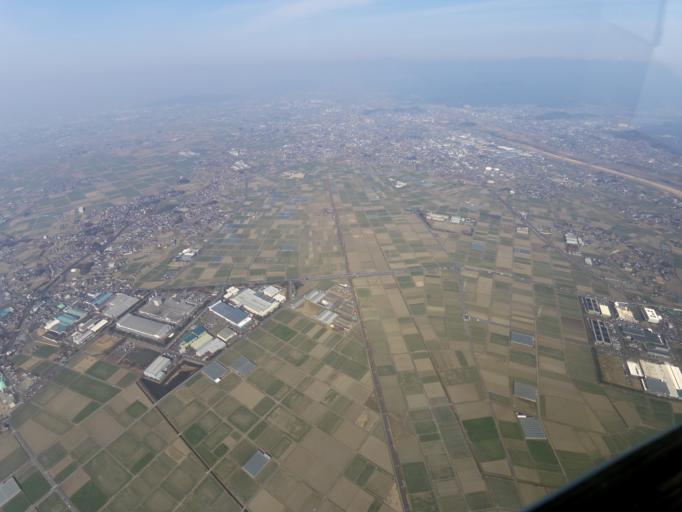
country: JP
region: Tochigi
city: Ashikaga
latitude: 36.2859
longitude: 139.4788
